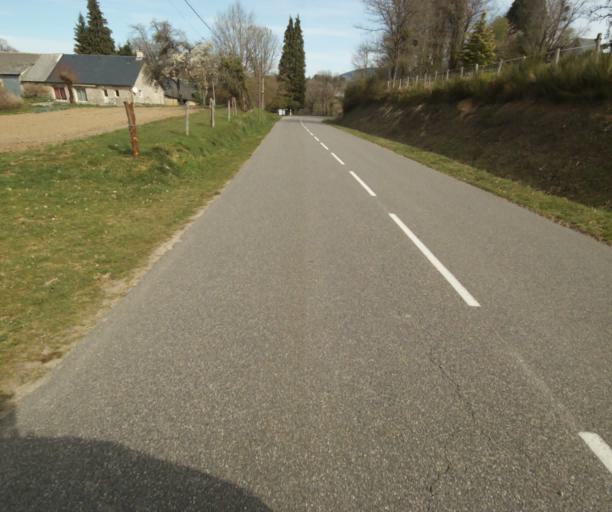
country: FR
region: Limousin
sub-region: Departement de la Correze
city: Correze
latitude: 45.4029
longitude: 1.8257
